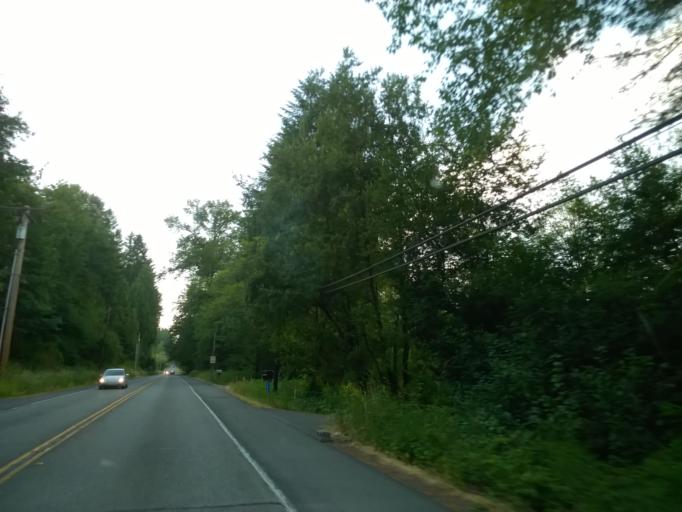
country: US
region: Washington
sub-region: King County
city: Cottage Lake
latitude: 47.7201
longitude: -122.0869
